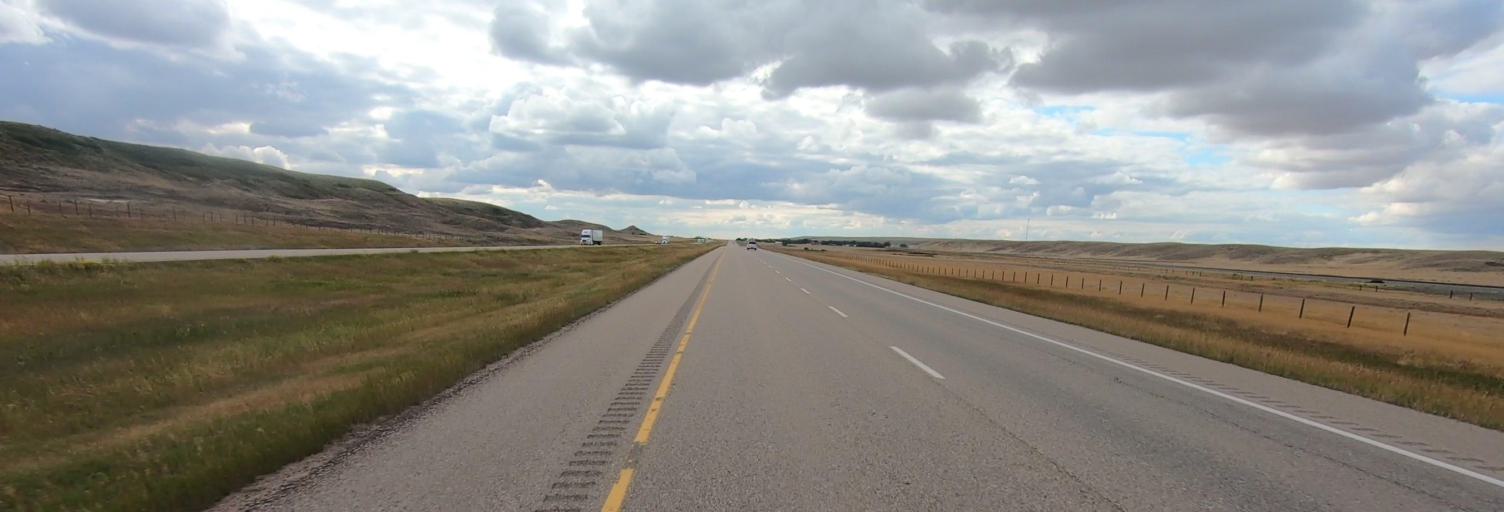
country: CA
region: Alberta
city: Medicine Hat
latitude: 49.9512
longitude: -110.2369
